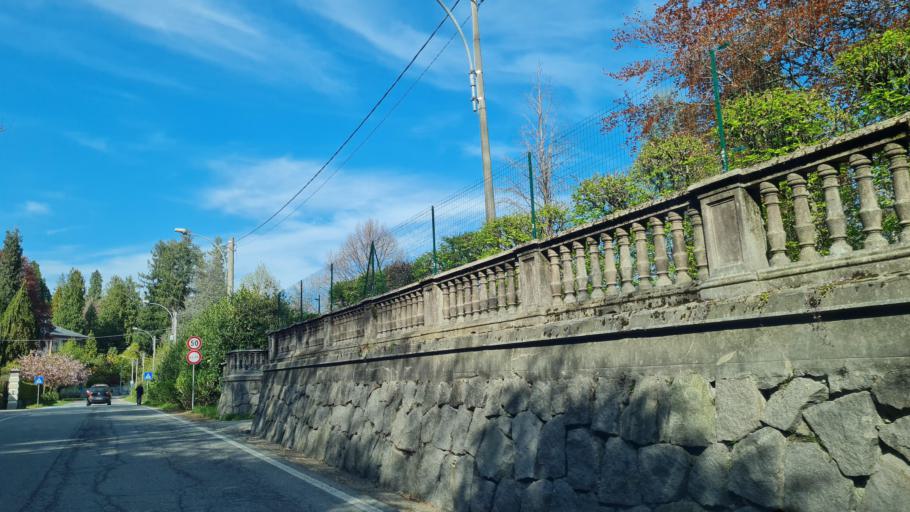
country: IT
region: Piedmont
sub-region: Provincia di Biella
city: Sordevolo
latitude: 45.5729
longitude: 7.9772
